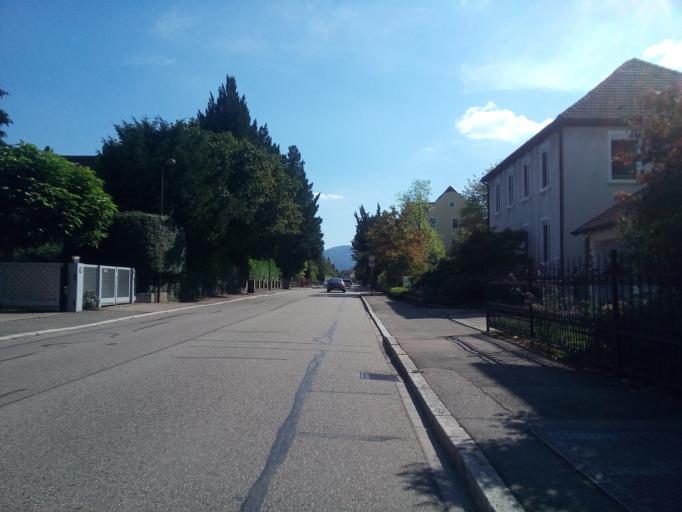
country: DE
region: Baden-Wuerttemberg
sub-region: Freiburg Region
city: Achern
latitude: 48.6258
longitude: 8.0759
